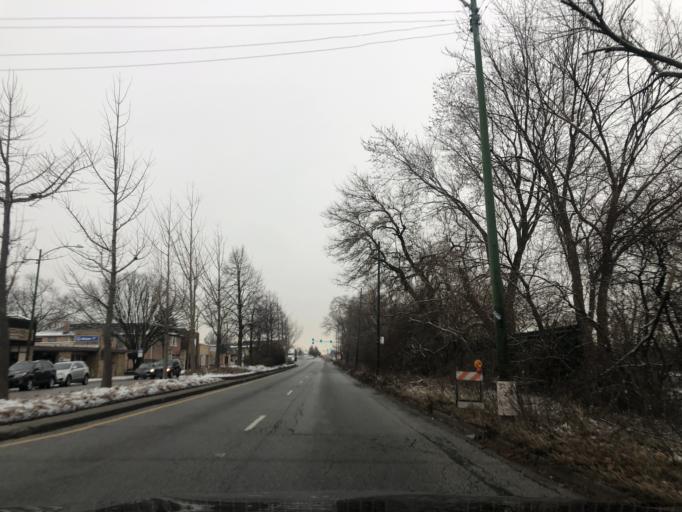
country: US
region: Illinois
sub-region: Cook County
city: Evergreen Park
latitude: 41.7302
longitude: -87.6825
